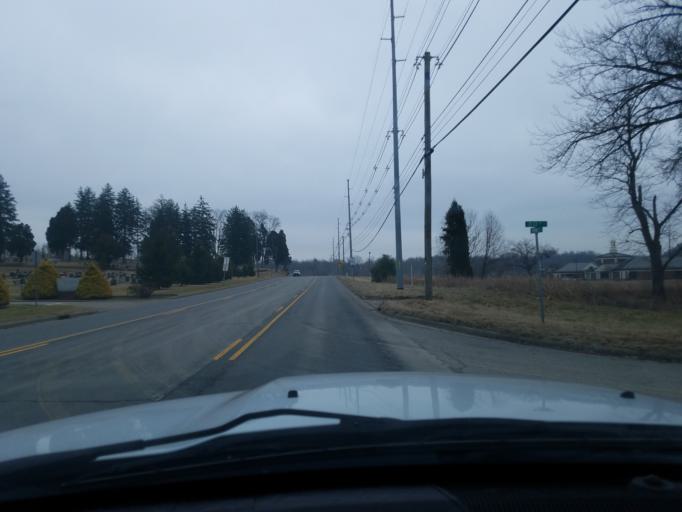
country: US
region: Indiana
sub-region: Perry County
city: Tell City
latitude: 37.9628
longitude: -86.7528
